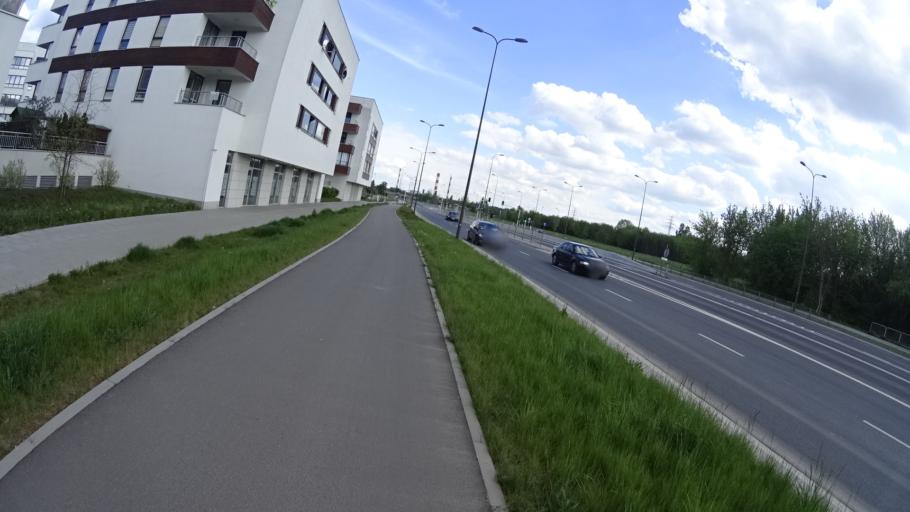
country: PL
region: Masovian Voivodeship
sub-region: Warszawa
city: Mokotow
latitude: 52.2071
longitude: 21.0620
